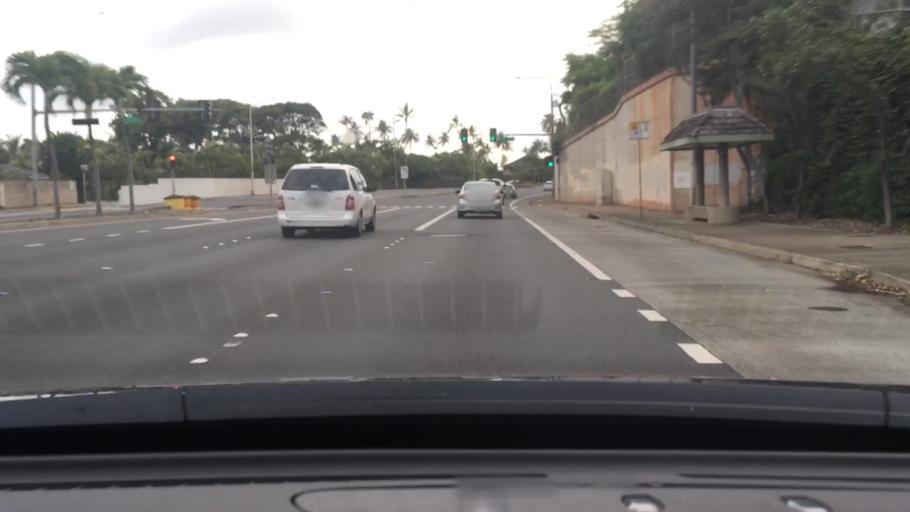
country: US
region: Hawaii
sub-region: Honolulu County
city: Waimanalo Beach
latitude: 21.2832
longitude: -157.7301
